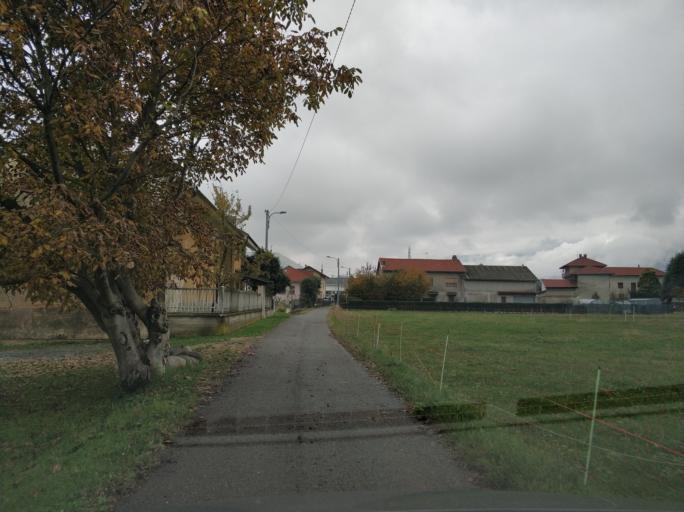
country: IT
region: Piedmont
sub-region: Provincia di Torino
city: Villanova Canavese
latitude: 45.2478
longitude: 7.5458
